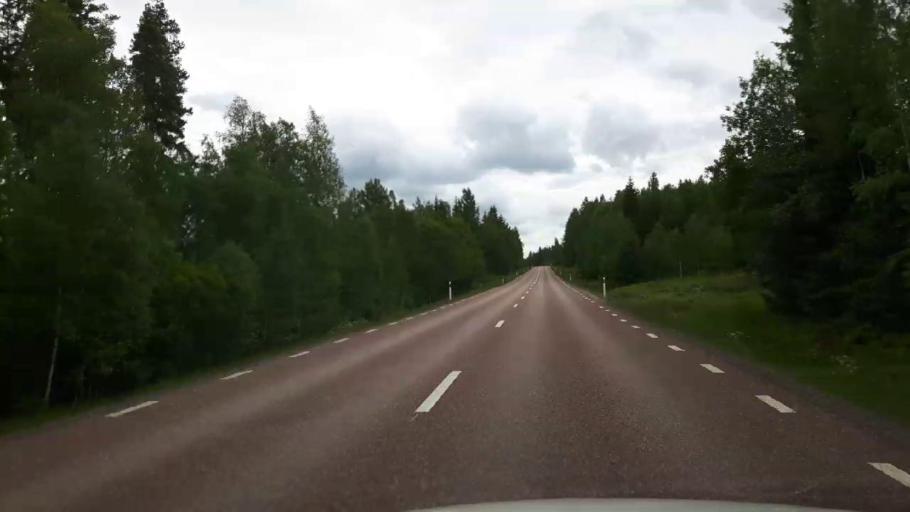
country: SE
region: Dalarna
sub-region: Hedemora Kommun
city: Brunna
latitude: 60.1989
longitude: 15.9954
